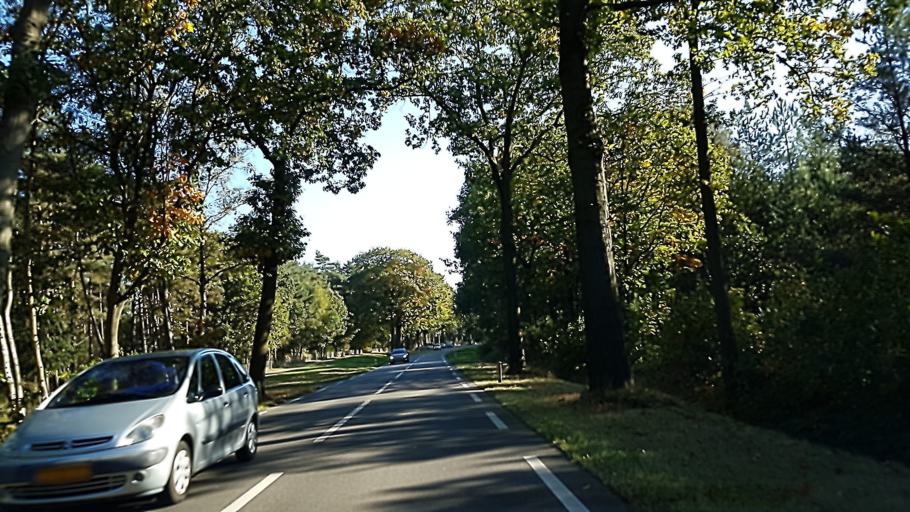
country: BE
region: Flanders
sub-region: Provincie Antwerpen
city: Stabroek
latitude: 51.3800
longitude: 4.3776
